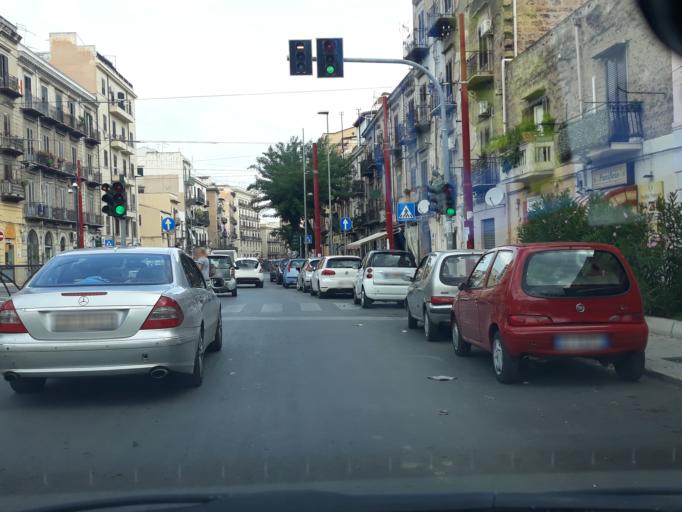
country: IT
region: Sicily
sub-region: Palermo
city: Palermo
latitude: 38.1104
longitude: 13.3695
